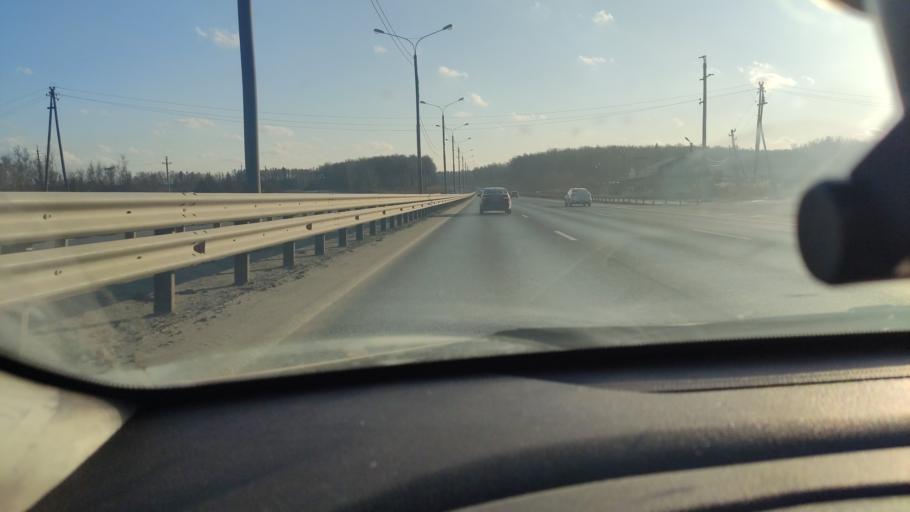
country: RU
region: Moskovskaya
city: Lyubuchany
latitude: 55.2528
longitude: 37.5314
